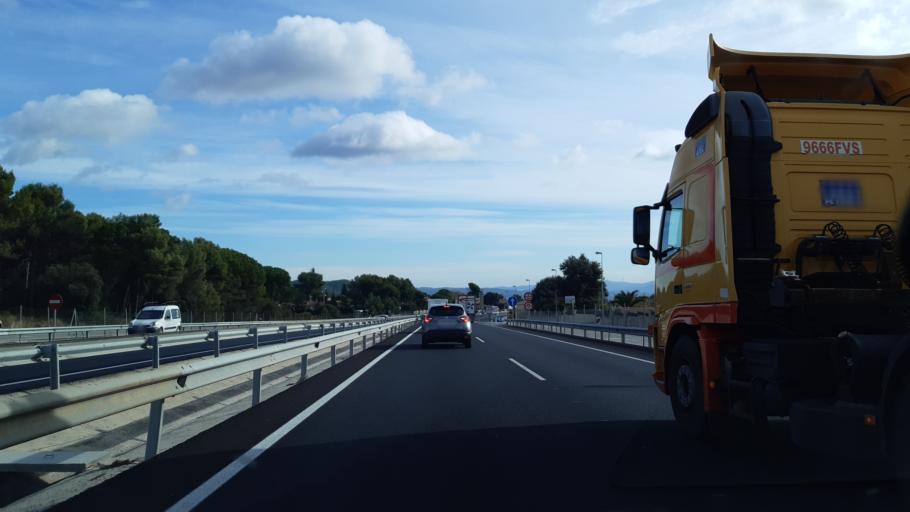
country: ES
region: Catalonia
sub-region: Provincia de Barcelona
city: Collbato
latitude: 41.5680
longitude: 1.8051
